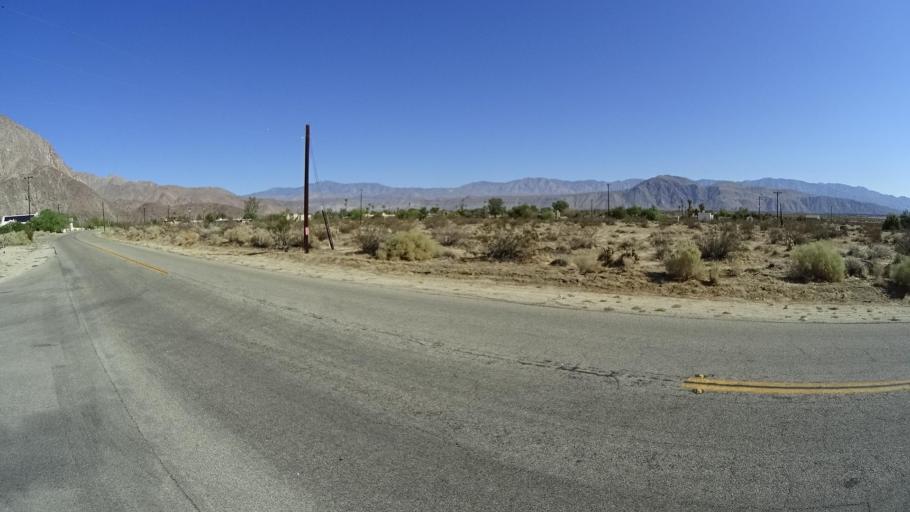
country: US
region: California
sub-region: San Diego County
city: Borrego Springs
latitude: 33.2761
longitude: -116.3915
